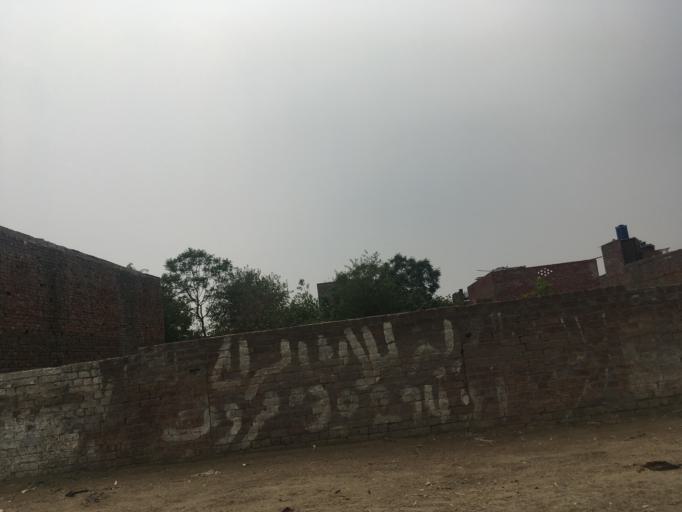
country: PK
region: Punjab
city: Lahore
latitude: 31.6205
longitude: 74.3468
